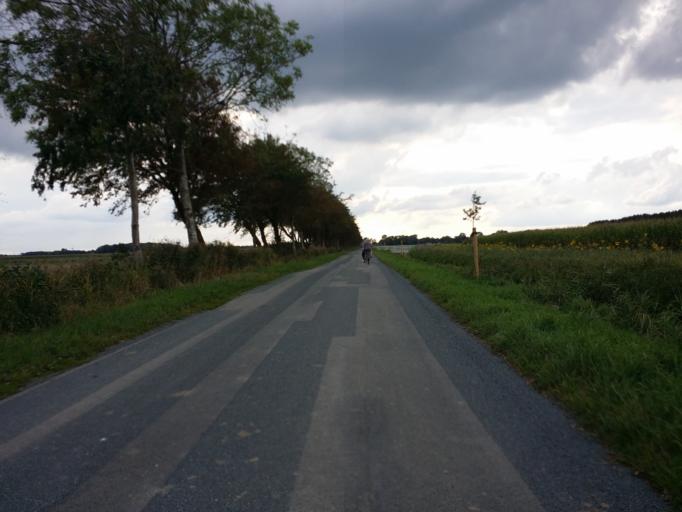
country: DE
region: Lower Saxony
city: Osten
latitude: 53.7343
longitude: 9.2001
